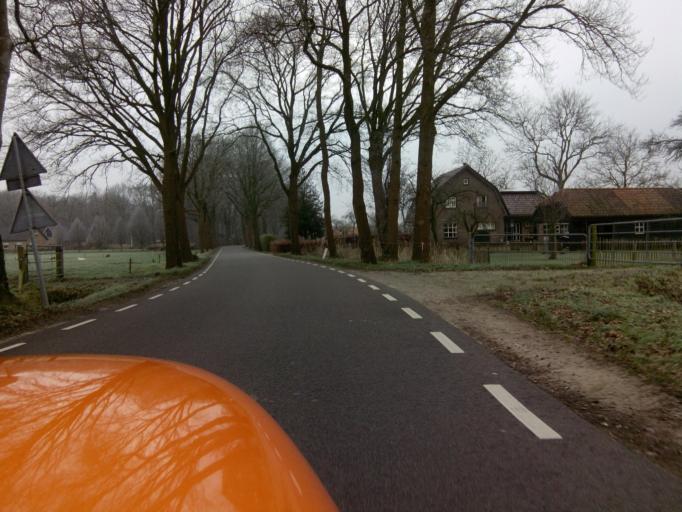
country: NL
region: Utrecht
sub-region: Gemeente Leusden
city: Leusden
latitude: 52.1613
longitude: 5.4592
